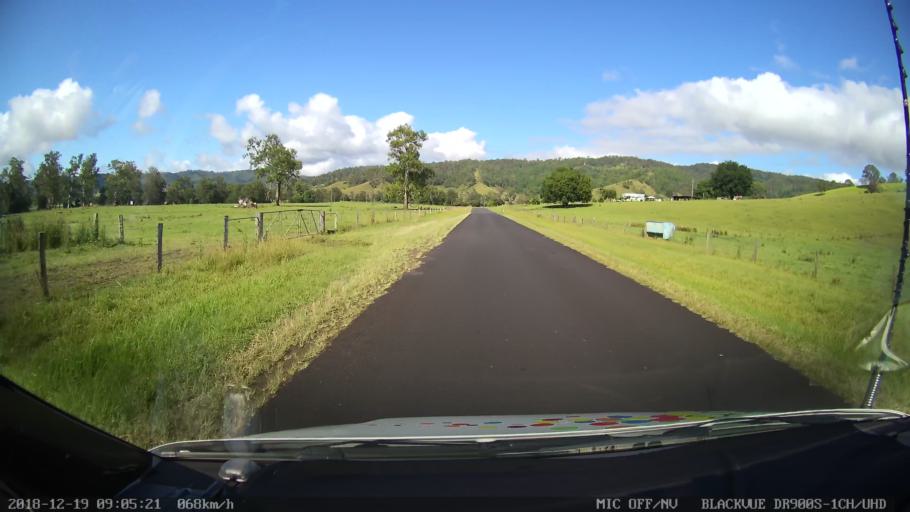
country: AU
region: New South Wales
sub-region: Kyogle
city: Kyogle
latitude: -28.4635
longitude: 152.9437
